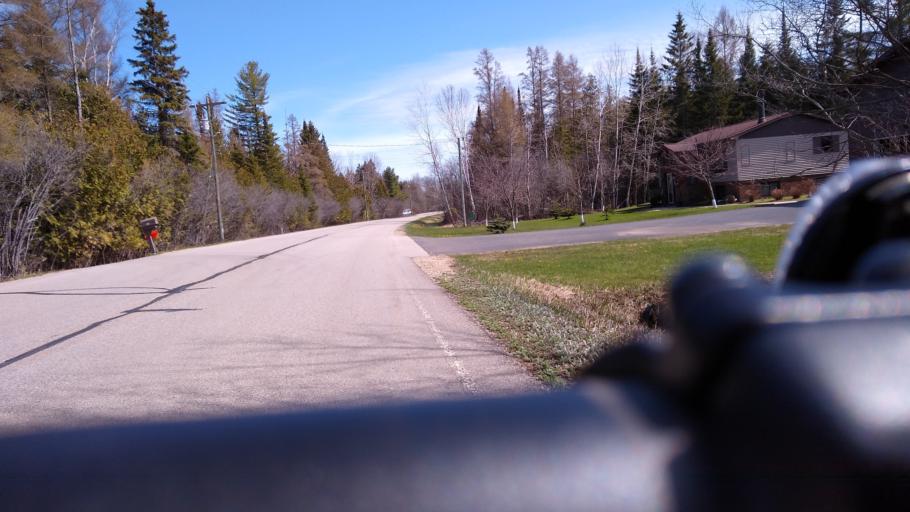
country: US
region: Michigan
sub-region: Delta County
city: Escanaba
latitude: 45.6833
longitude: -87.1465
